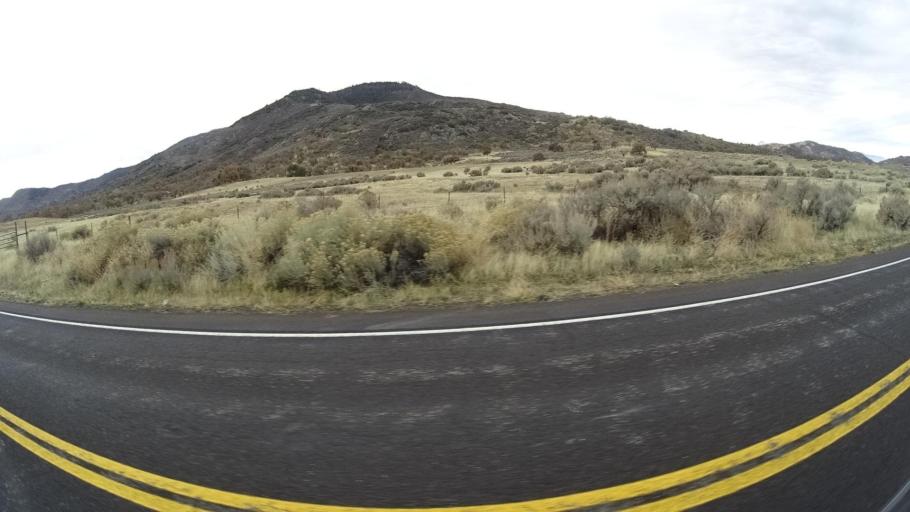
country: US
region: California
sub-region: Kern County
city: Stallion Springs
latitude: 35.0949
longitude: -118.5879
